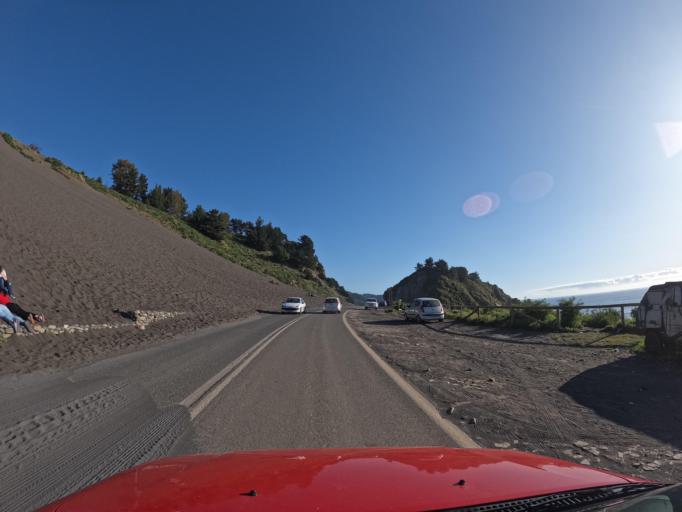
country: CL
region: Maule
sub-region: Provincia de Talca
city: Constitucion
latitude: -35.3379
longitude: -72.4343
